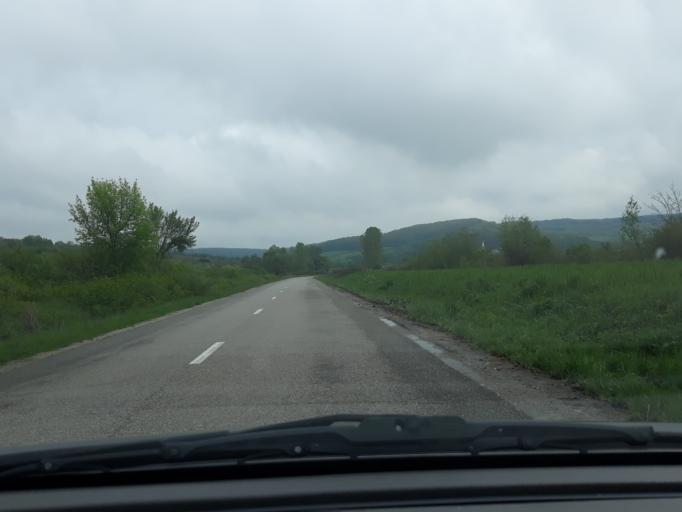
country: RO
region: Salaj
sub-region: Comuna Dobrin
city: Dobrin
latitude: 47.2949
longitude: 23.1167
